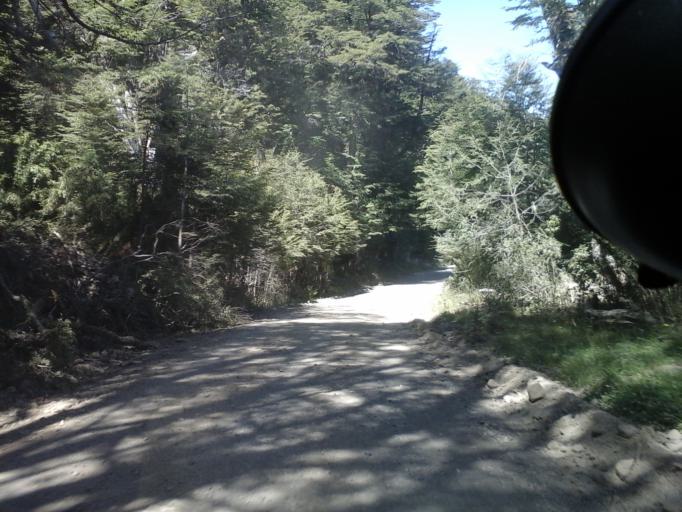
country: AR
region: Neuquen
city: Villa La Angostura
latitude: -41.2120
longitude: -71.8062
